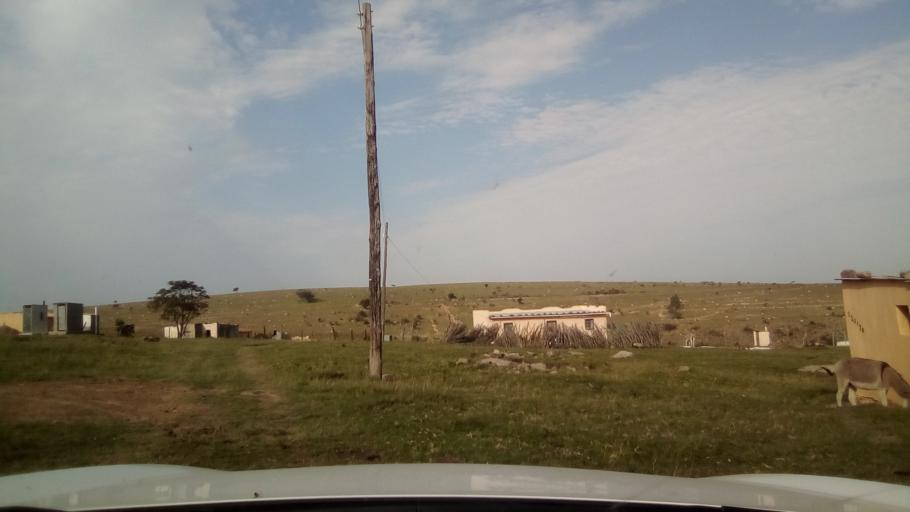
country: ZA
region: Eastern Cape
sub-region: Buffalo City Metropolitan Municipality
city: Bhisho
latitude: -33.0108
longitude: 27.3061
